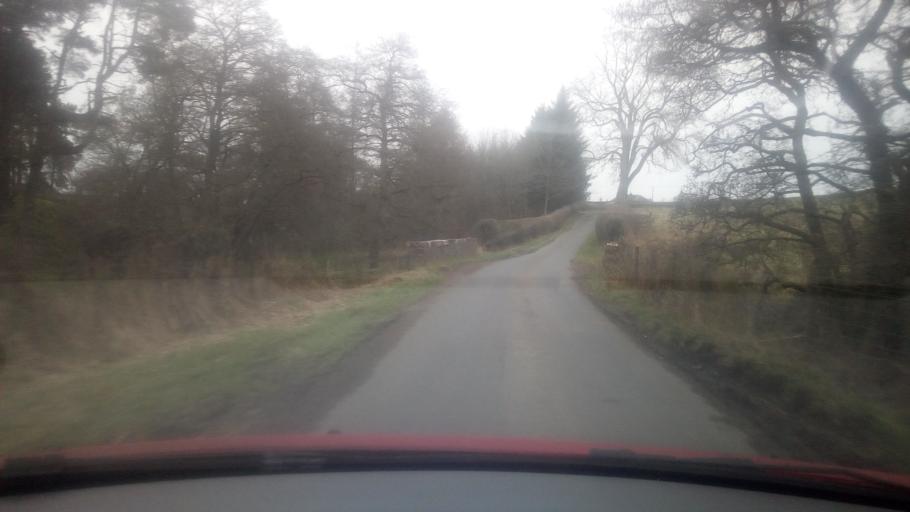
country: GB
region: Scotland
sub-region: The Scottish Borders
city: Hawick
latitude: 55.4387
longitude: -2.6905
